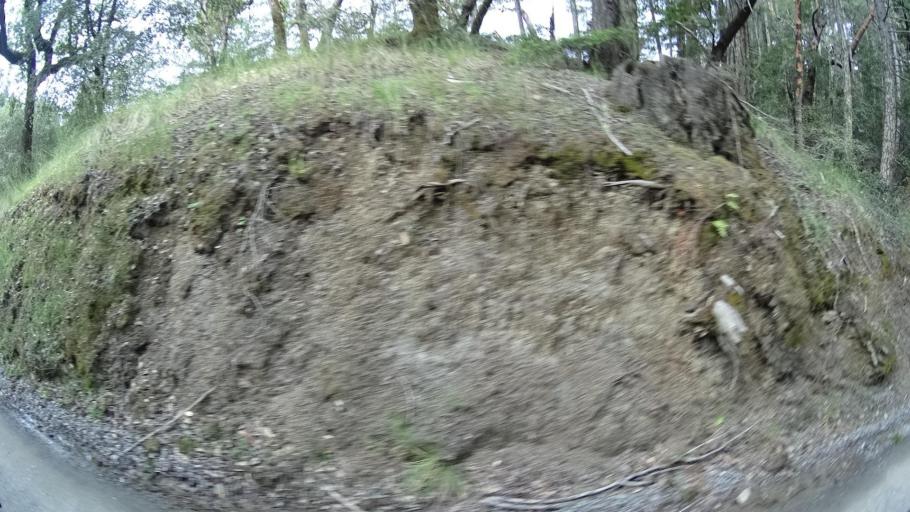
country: US
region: California
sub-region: Humboldt County
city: Redway
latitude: 40.0521
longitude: -123.8372
